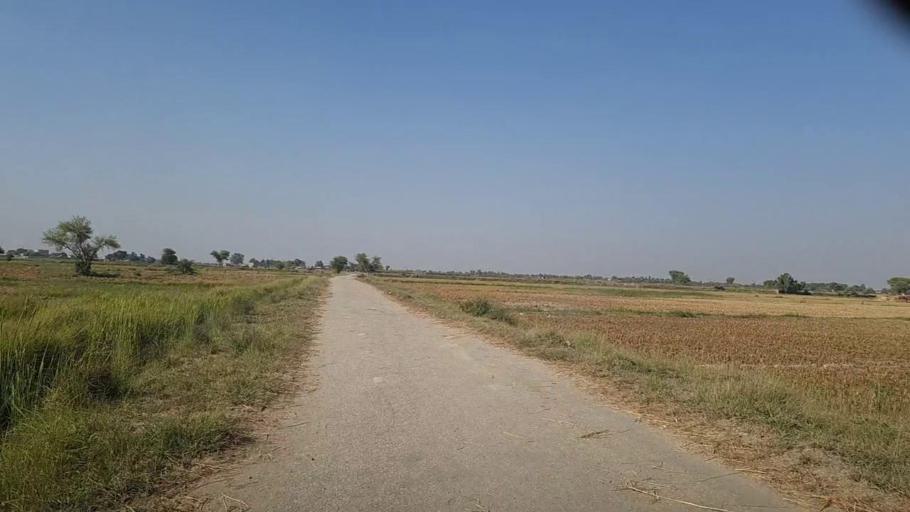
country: PK
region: Sindh
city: Tangwani
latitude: 28.2620
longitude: 68.9341
